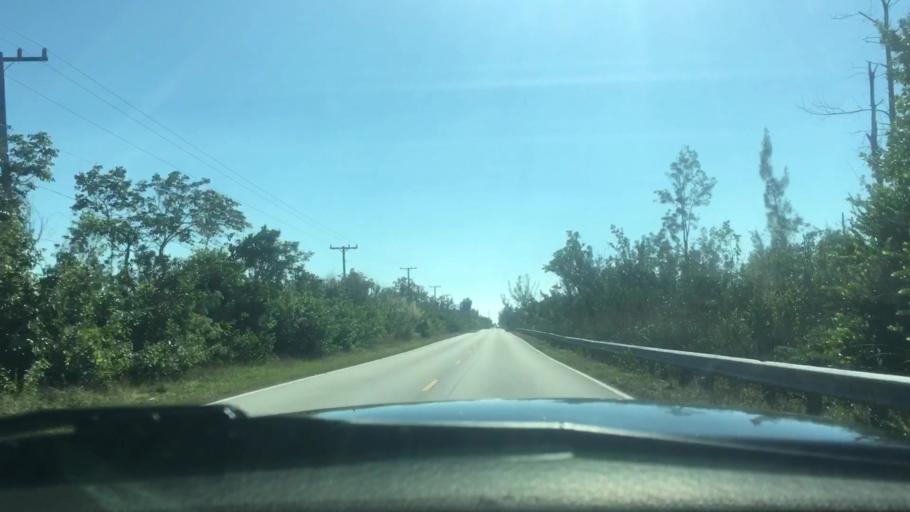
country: US
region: Florida
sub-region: Miami-Dade County
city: Florida City
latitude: 25.3709
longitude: -80.4325
